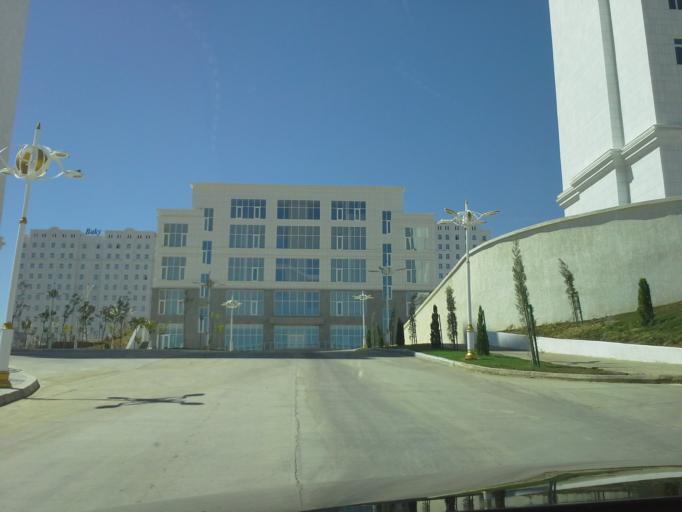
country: TM
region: Ahal
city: Ashgabat
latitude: 37.9428
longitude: 58.3484
